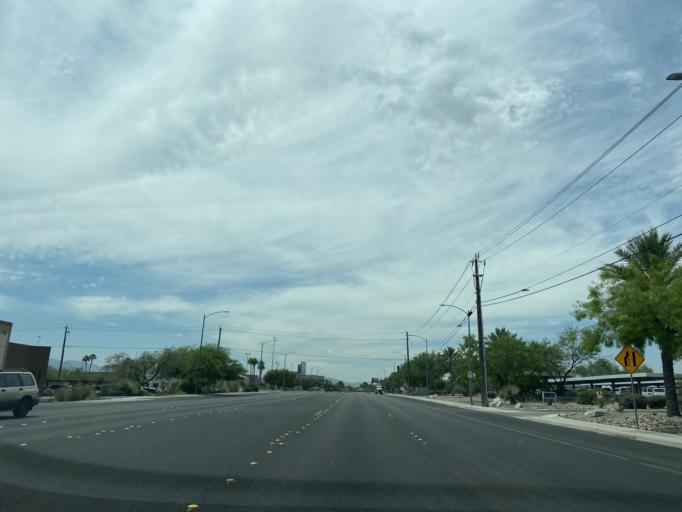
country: US
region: Nevada
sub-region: Clark County
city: Paradise
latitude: 36.0671
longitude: -115.1545
